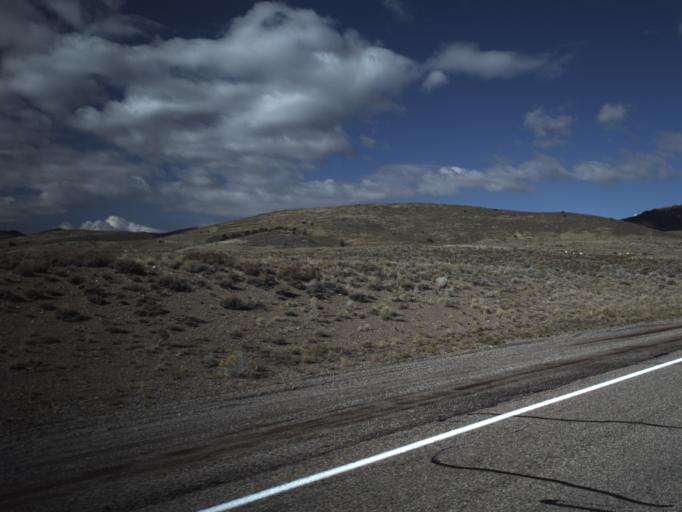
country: US
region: Utah
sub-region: Beaver County
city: Milford
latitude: 38.4565
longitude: -113.2185
